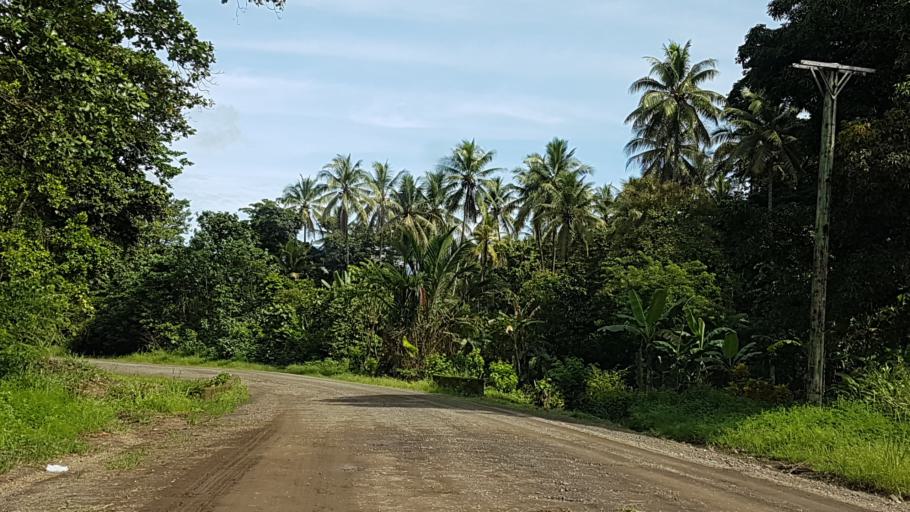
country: PG
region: Milne Bay
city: Alotau
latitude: -10.3250
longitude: 150.5056
